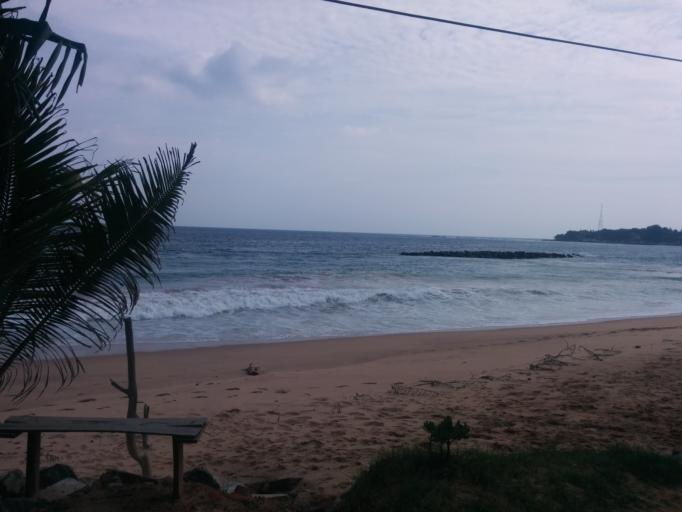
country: LK
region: Southern
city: Tangalla
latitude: 6.0351
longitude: 80.8026
